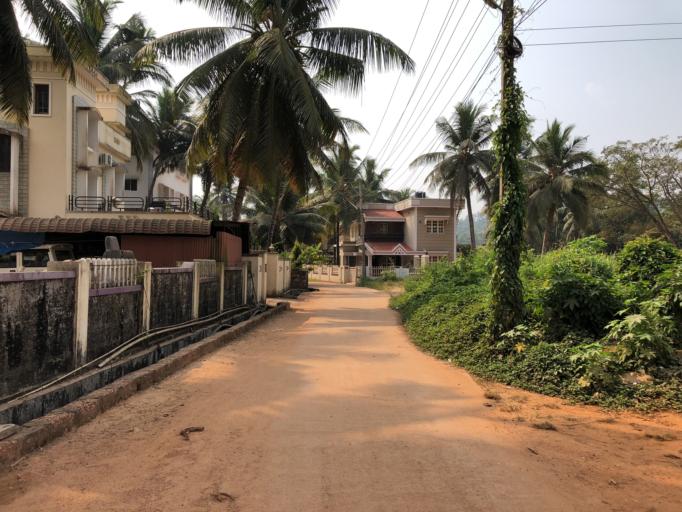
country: IN
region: Karnataka
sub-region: Dakshina Kannada
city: Mangalore
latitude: 12.8709
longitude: 74.8928
